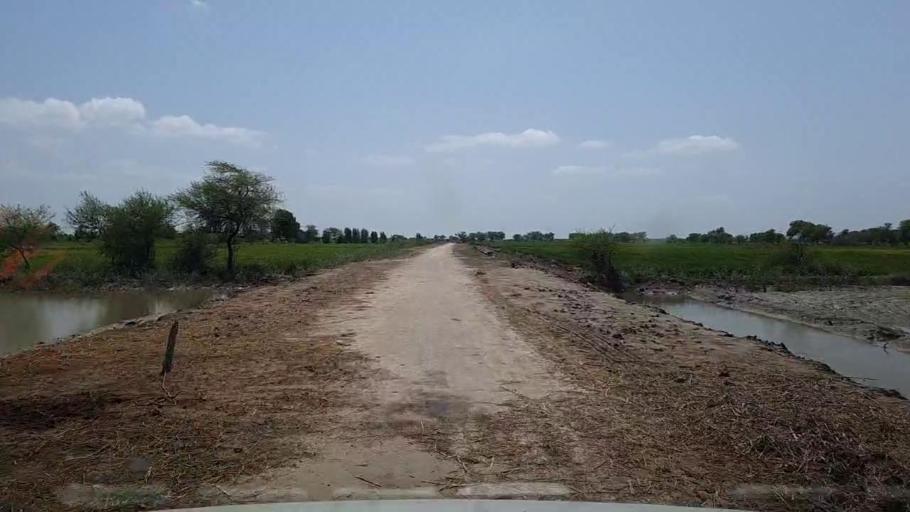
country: PK
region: Sindh
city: Kario
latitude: 24.6875
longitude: 68.5940
